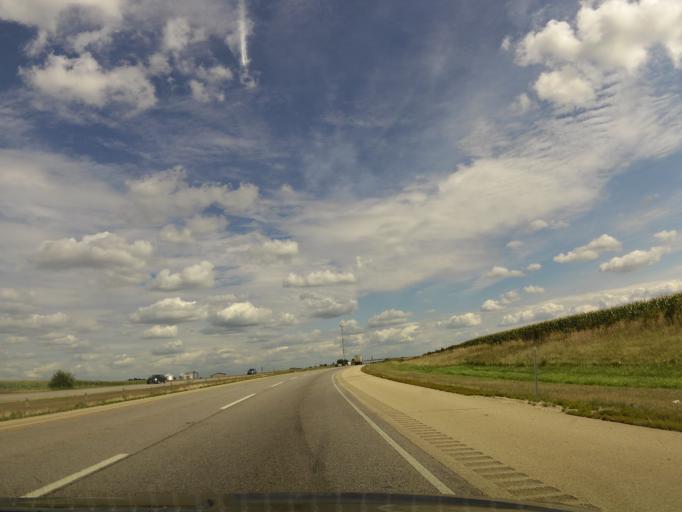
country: US
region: Illinois
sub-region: Ogle County
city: Rochelle
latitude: 41.9052
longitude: -88.9722
